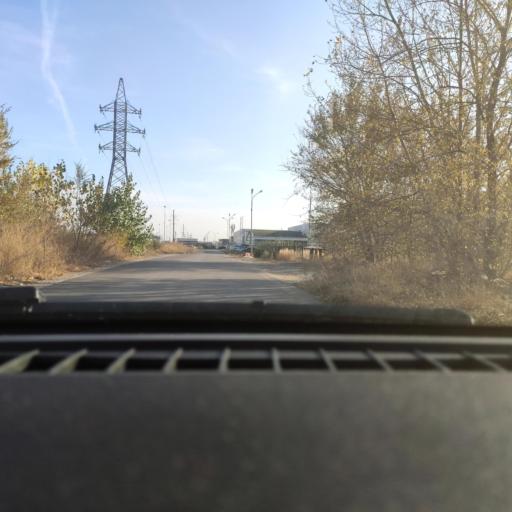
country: RU
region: Voronezj
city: Somovo
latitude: 51.6671
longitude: 39.2998
